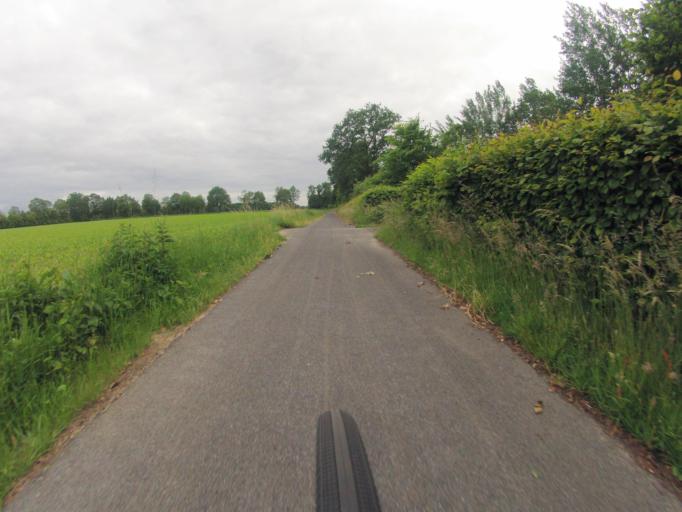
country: DE
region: North Rhine-Westphalia
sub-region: Regierungsbezirk Munster
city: Birgte
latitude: 52.2084
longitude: 7.6730
